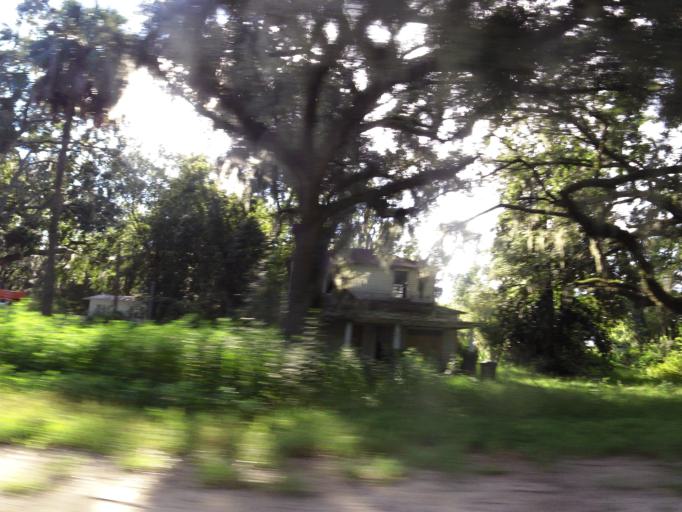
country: US
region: Georgia
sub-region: Glynn County
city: Country Club Estates
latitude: 31.2419
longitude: -81.4506
